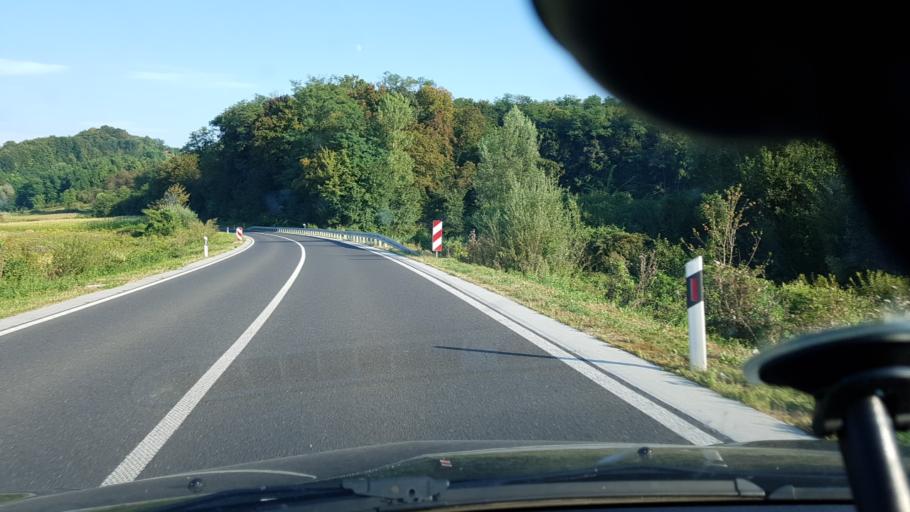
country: HR
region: Krapinsko-Zagorska
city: Zabok
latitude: 46.0306
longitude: 15.8324
